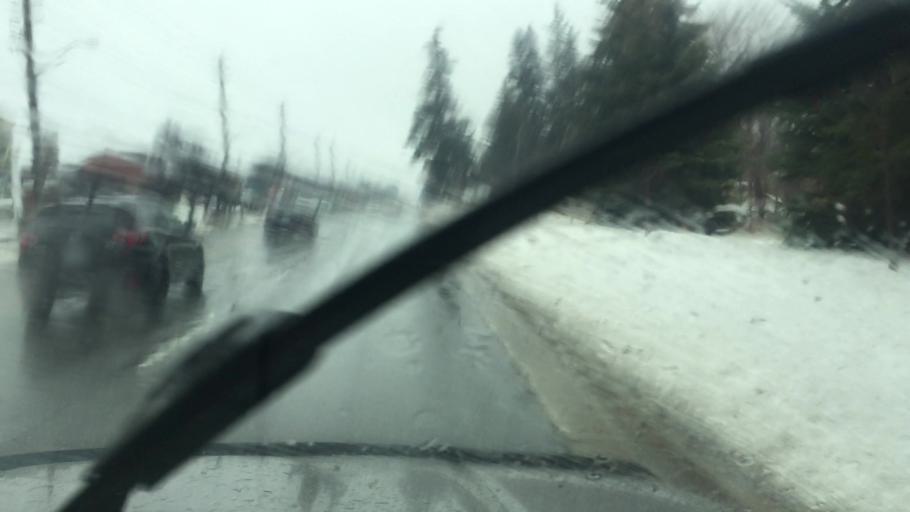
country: CA
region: Ontario
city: Ajax
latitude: 43.8534
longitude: -79.0601
